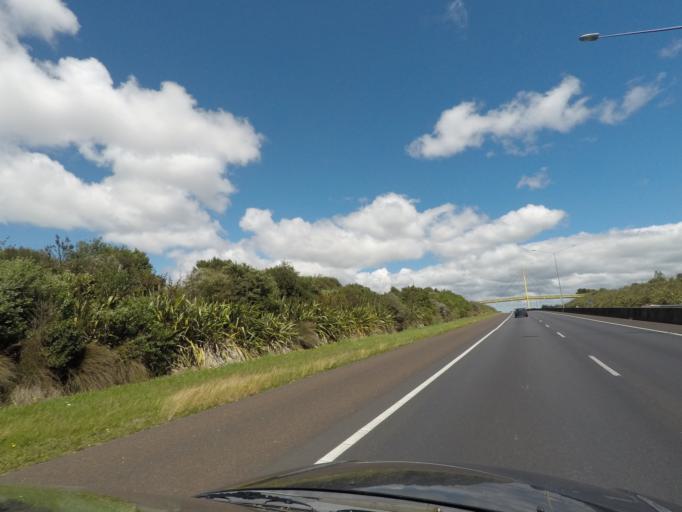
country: NZ
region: Auckland
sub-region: Auckland
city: Rosebank
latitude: -36.7943
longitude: 174.6493
